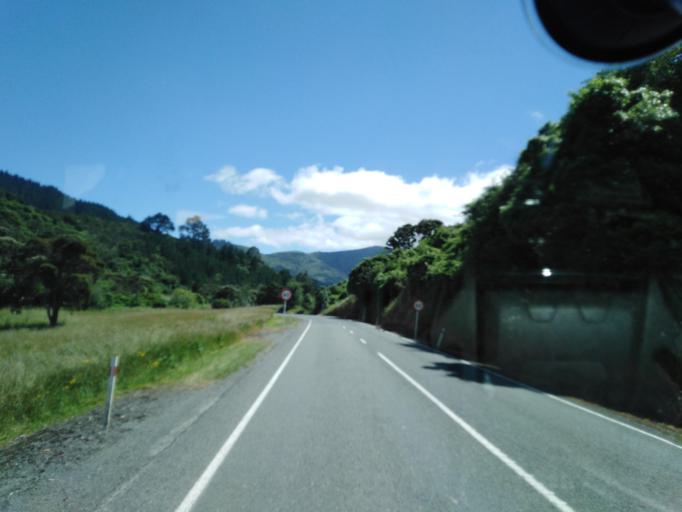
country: NZ
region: Nelson
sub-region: Nelson City
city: Nelson
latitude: -41.2279
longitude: 173.3975
